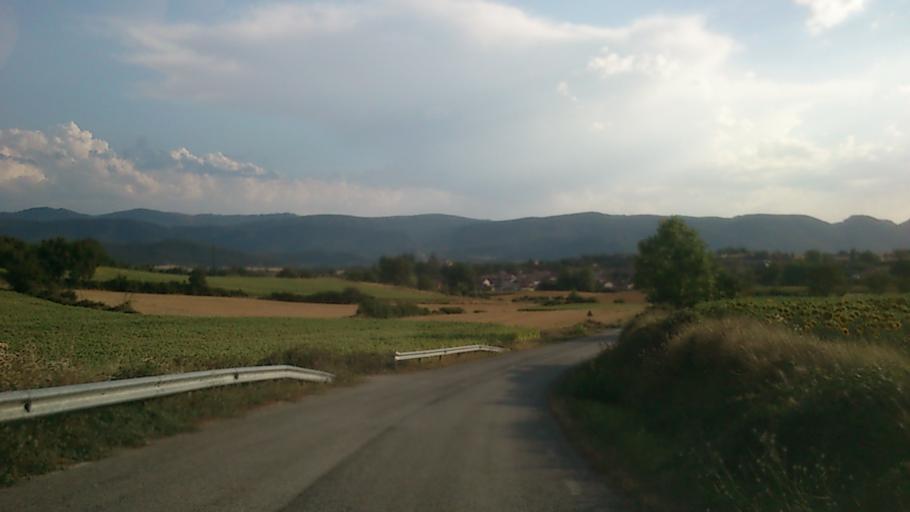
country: ES
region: Castille and Leon
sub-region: Provincia de Burgos
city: Frias
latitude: 42.7994
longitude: -3.2622
